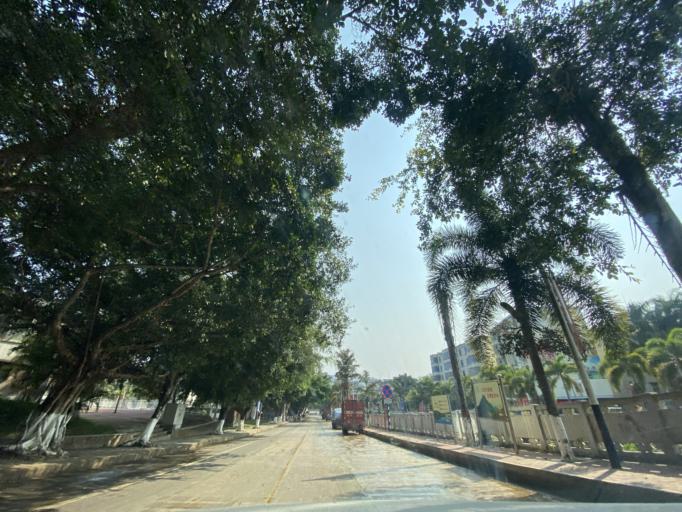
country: CN
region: Hainan
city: Chongshan
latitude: 18.7844
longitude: 109.5142
